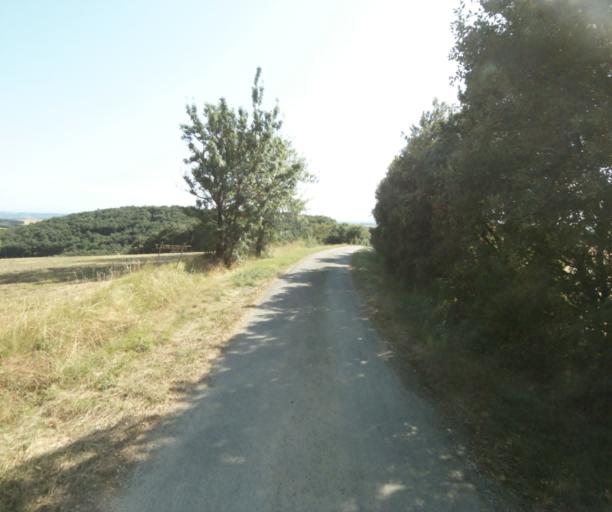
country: FR
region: Midi-Pyrenees
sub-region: Departement de la Haute-Garonne
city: Saint-Felix-Lauragais
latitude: 43.4207
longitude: 1.8444
